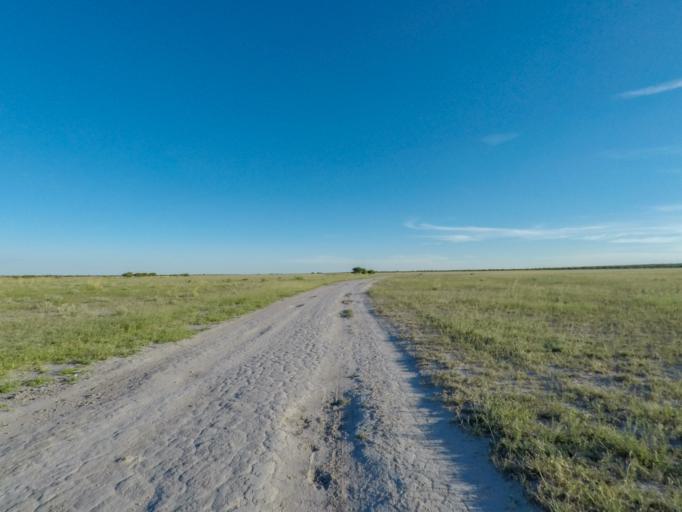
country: BW
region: Central
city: Rakops
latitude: -21.3896
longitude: 23.7942
